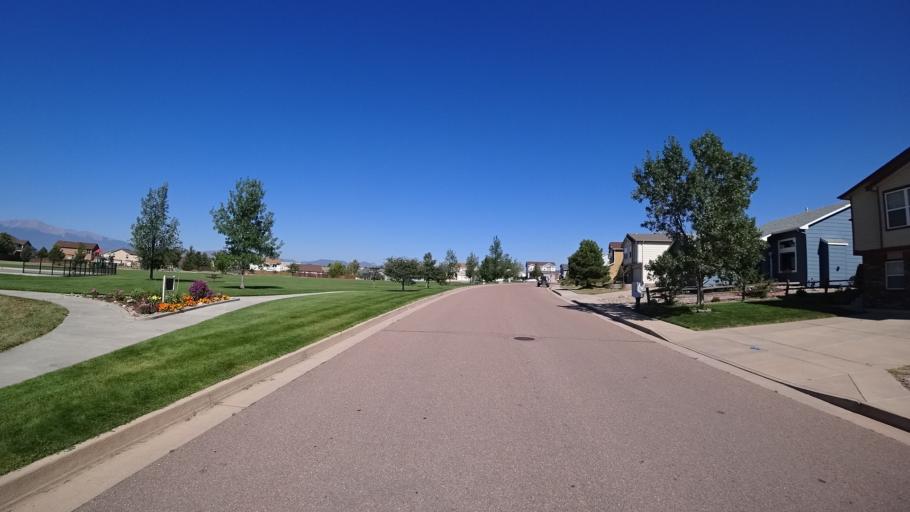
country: US
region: Colorado
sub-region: El Paso County
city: Black Forest
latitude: 38.9445
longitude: -104.7354
